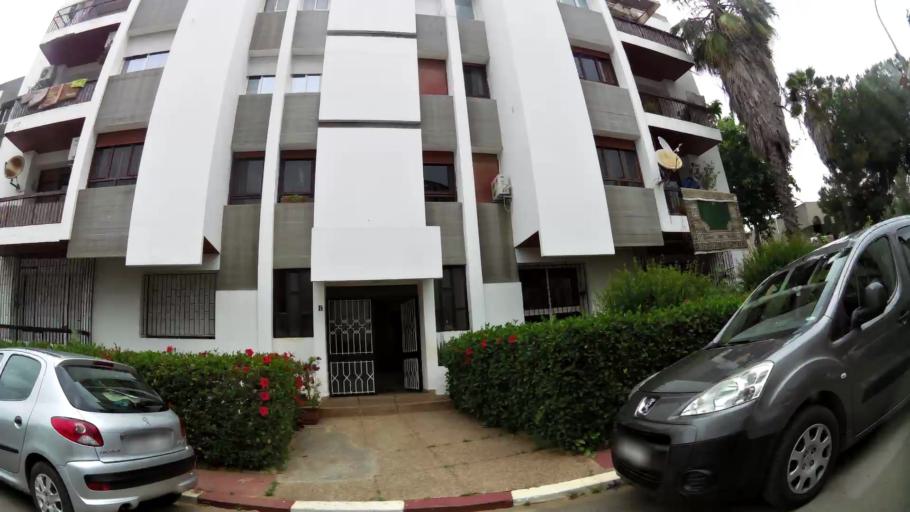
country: MA
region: Rabat-Sale-Zemmour-Zaer
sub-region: Rabat
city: Rabat
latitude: 33.9881
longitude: -6.8258
